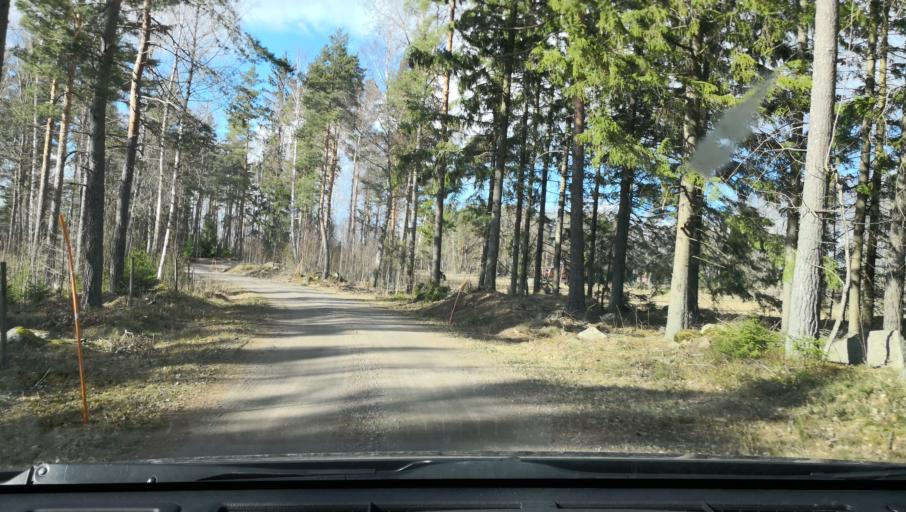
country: SE
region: OErebro
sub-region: Lindesbergs Kommun
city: Fellingsbro
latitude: 59.4293
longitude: 15.6868
